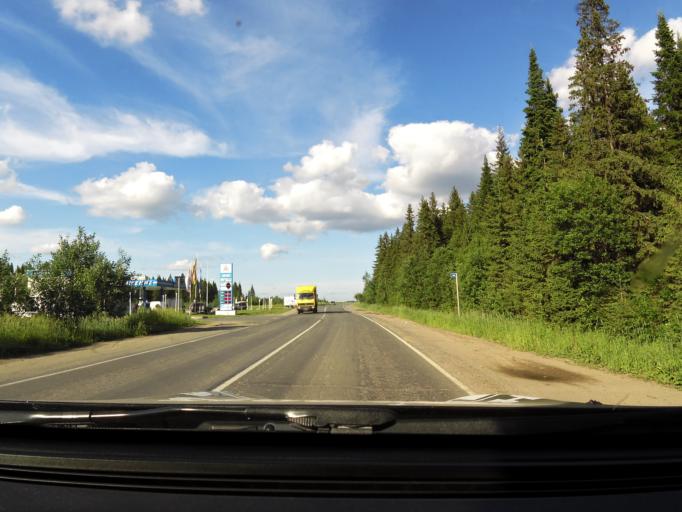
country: RU
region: Kirov
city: Omutninsk
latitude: 58.6850
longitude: 52.1476
